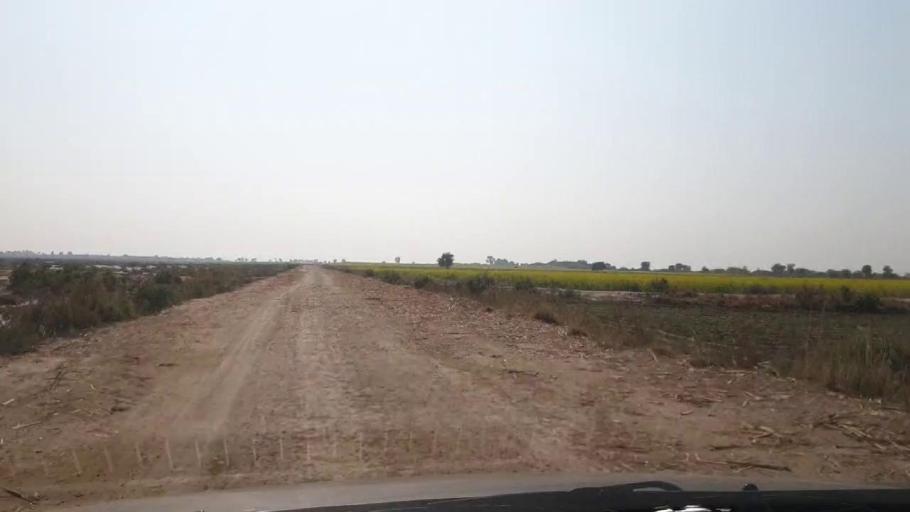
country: PK
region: Sindh
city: Jhol
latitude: 25.8734
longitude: 68.9977
